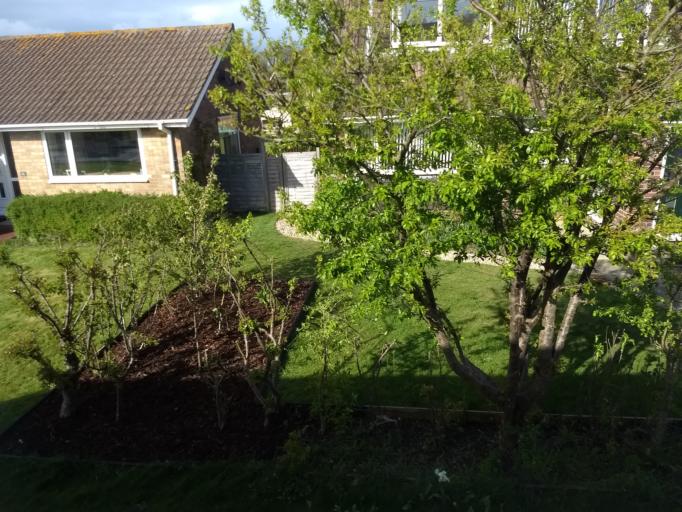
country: GB
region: England
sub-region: Isle of Wight
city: Seaview
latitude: 50.7152
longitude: -1.1129
